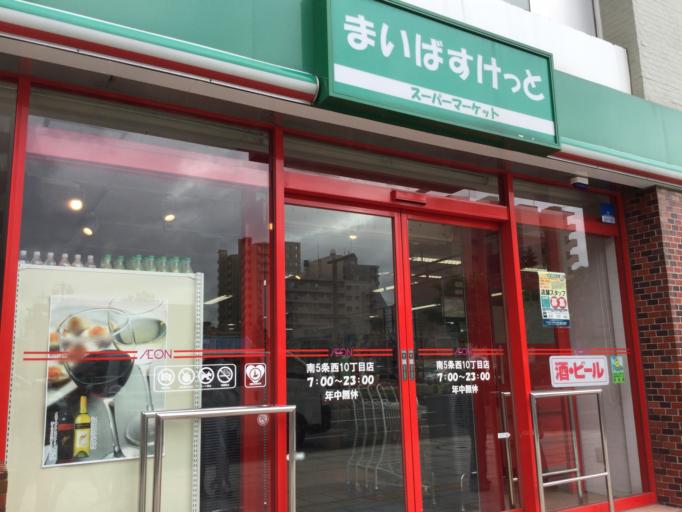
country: JP
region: Hokkaido
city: Sapporo
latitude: 43.0528
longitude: 141.3425
